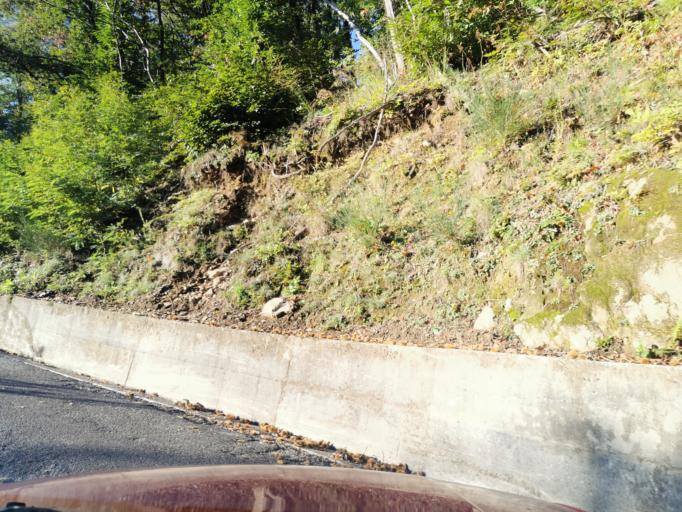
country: IT
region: Lombardy
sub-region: Provincia di Como
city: San Siro
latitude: 46.0679
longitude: 9.2570
